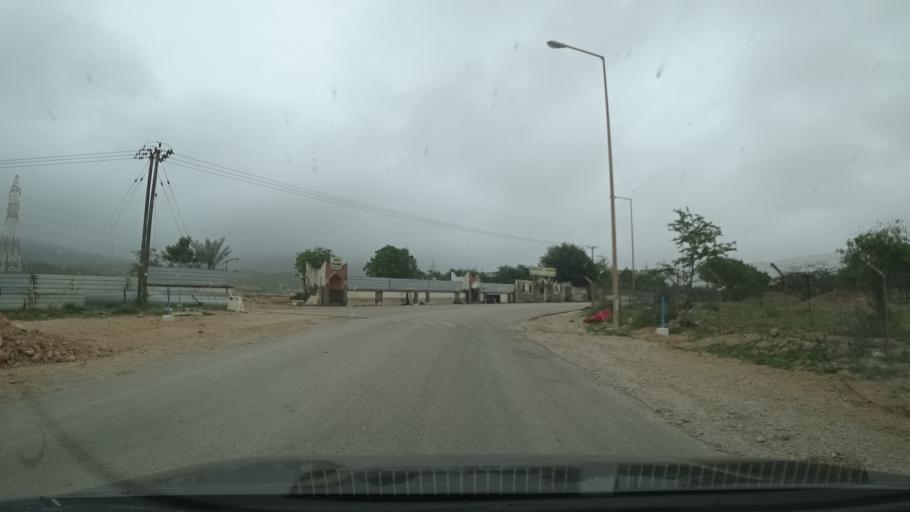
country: OM
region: Zufar
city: Salalah
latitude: 17.0854
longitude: 54.0709
